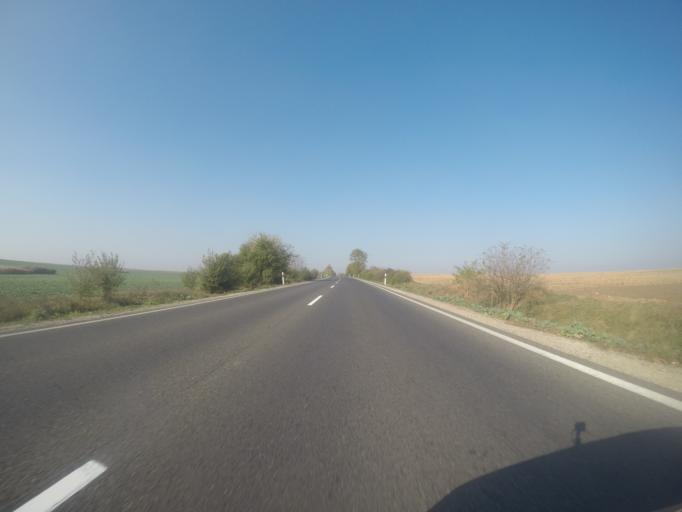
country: HU
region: Fejer
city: Racalmas
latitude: 47.0062
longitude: 18.9305
